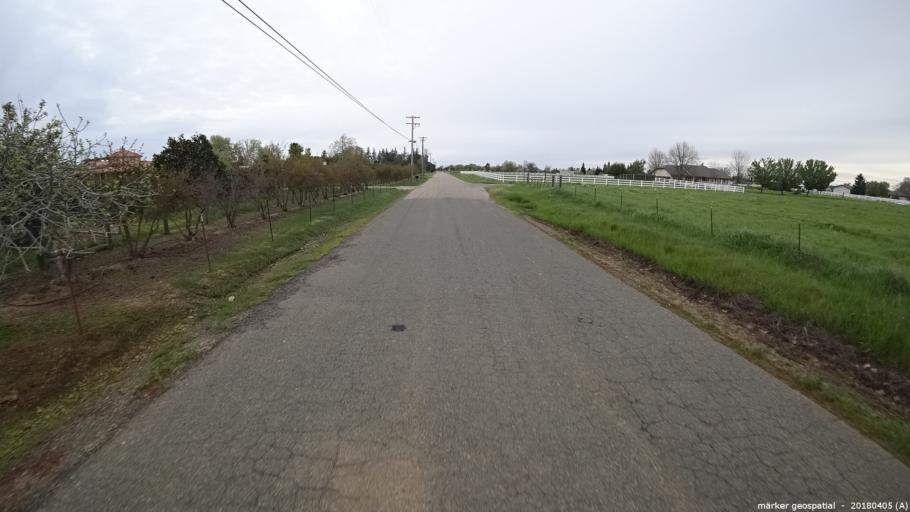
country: US
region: California
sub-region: Sacramento County
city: Herald
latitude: 38.2857
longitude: -121.2357
